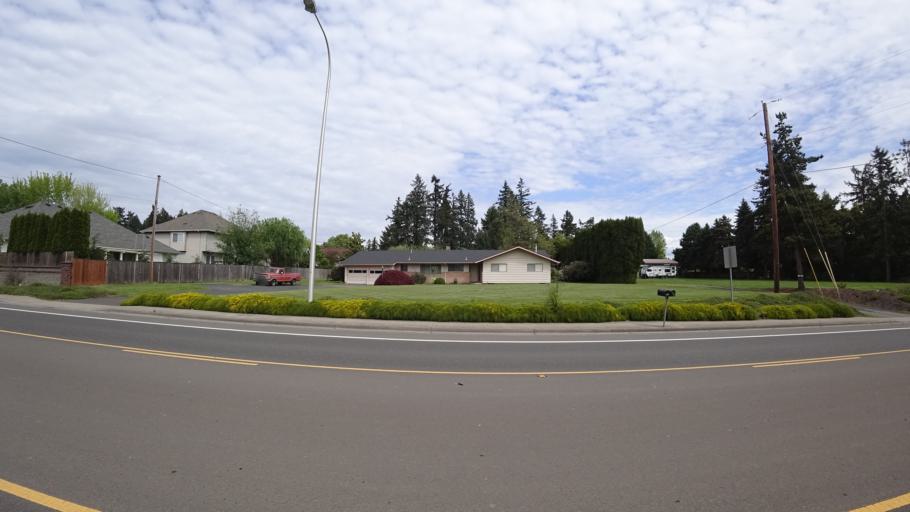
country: US
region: Oregon
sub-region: Washington County
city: Hillsboro
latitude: 45.5101
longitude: -122.9367
